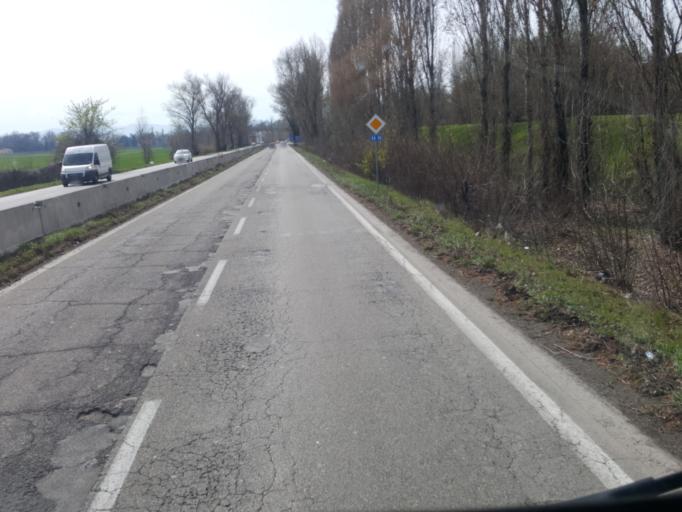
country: IT
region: Emilia-Romagna
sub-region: Provincia di Modena
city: Modena
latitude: 44.6481
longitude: 10.9627
